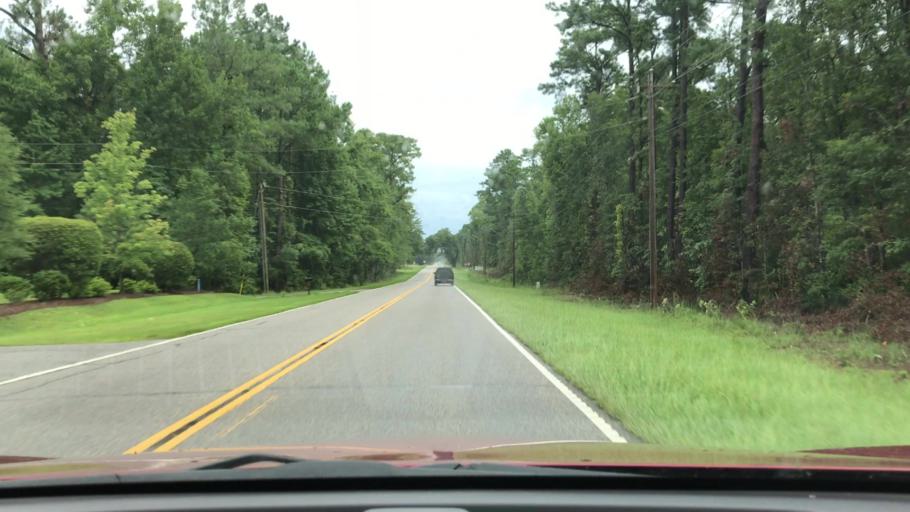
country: US
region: South Carolina
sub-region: Georgetown County
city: Georgetown
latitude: 33.4603
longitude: -79.2810
